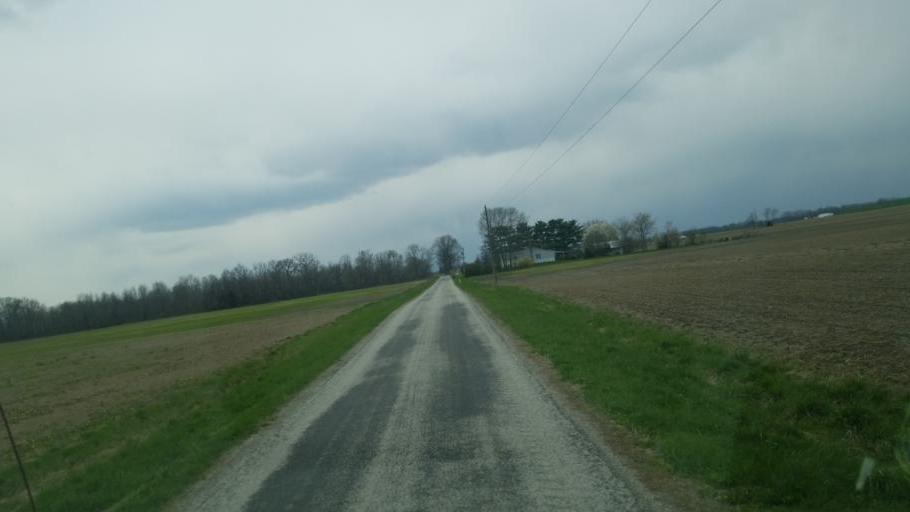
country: US
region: Ohio
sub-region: Marion County
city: Prospect
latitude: 40.3846
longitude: -83.2290
